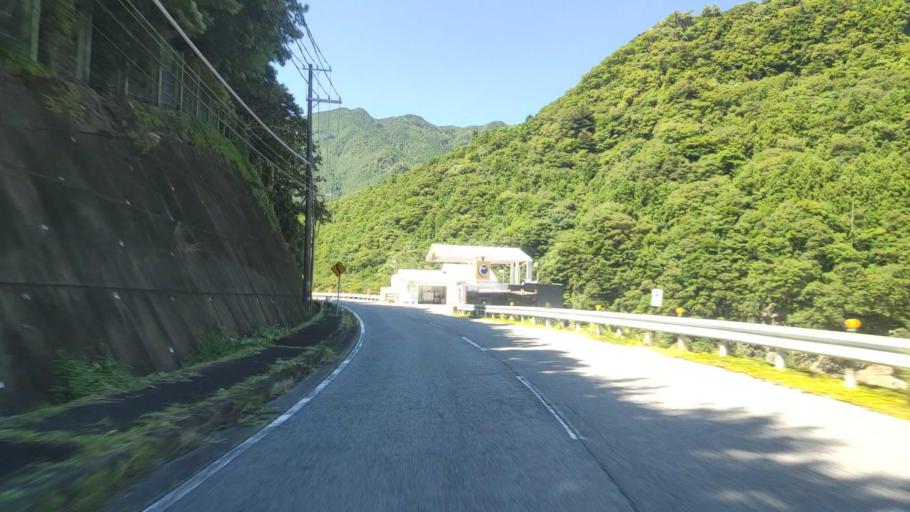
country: JP
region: Nara
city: Yoshino-cho
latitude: 34.3216
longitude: 135.9707
